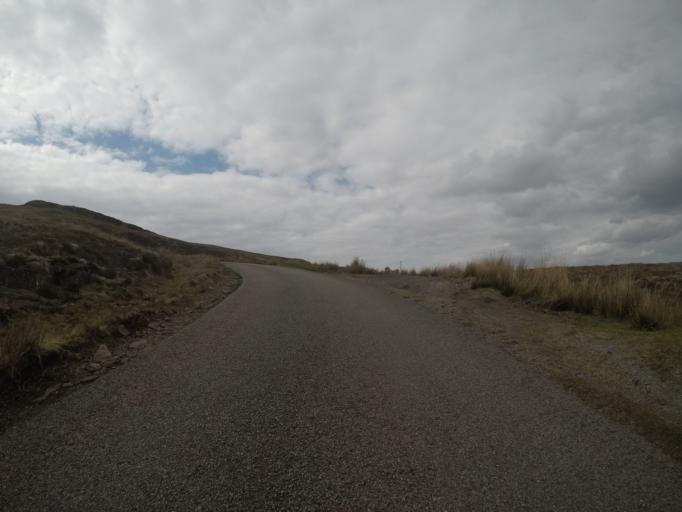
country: GB
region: Scotland
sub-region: Highland
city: Isle of Skye
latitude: 57.2960
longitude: -6.3609
